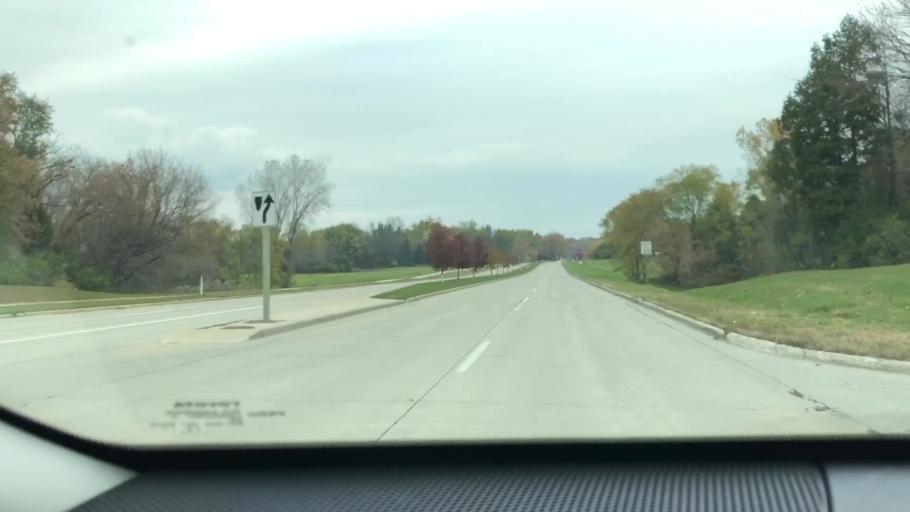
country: US
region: Wisconsin
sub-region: Brown County
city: Ashwaubenon
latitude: 44.4972
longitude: -88.1036
